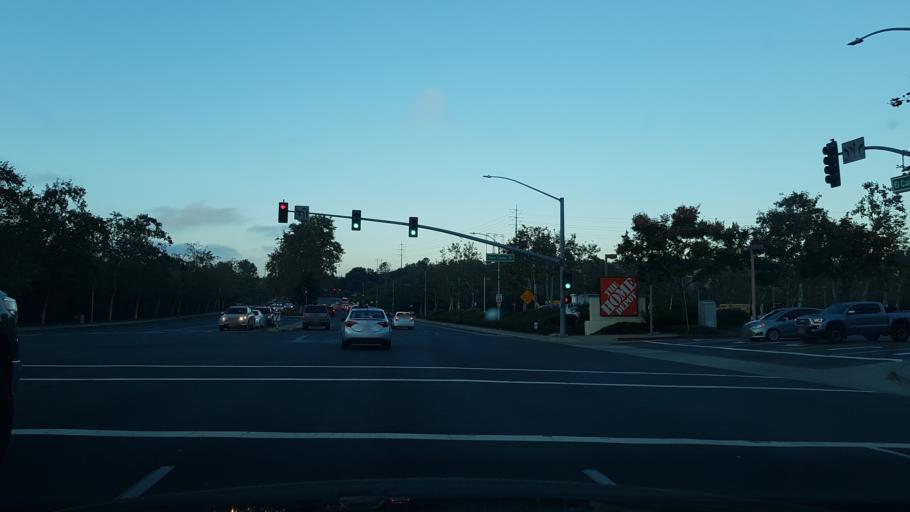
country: US
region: California
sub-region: San Diego County
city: Encinitas
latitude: 33.0646
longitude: -117.2623
